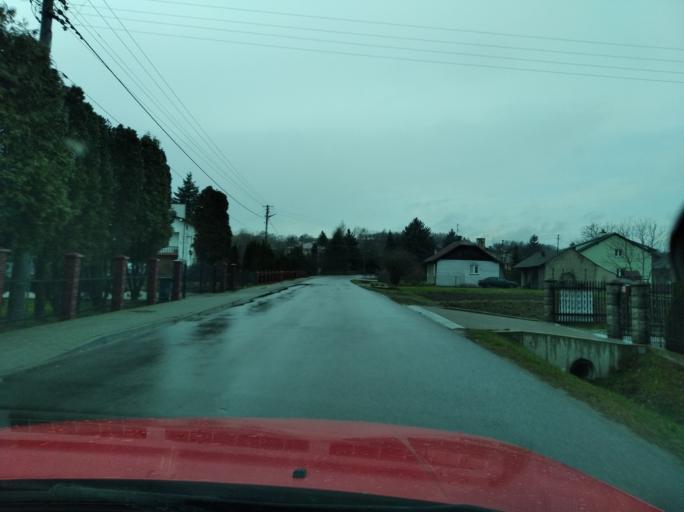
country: PL
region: Subcarpathian Voivodeship
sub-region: Powiat rzeszowski
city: Lutoryz
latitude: 49.9507
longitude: 21.9197
